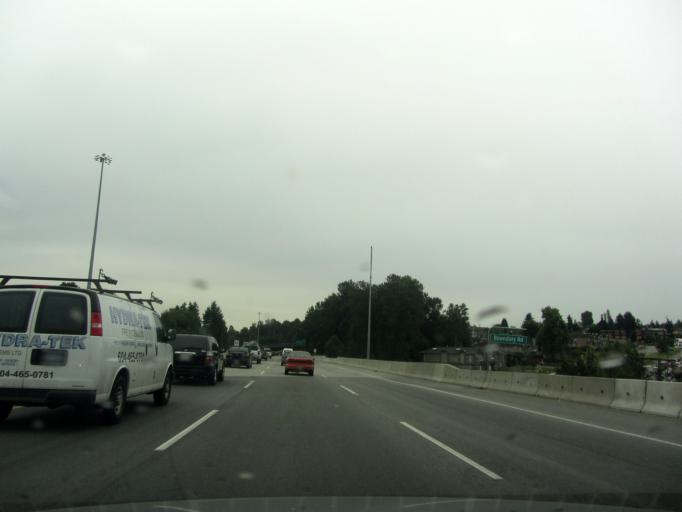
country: CA
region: British Columbia
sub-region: Fraser Valley Regional District
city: North Vancouver
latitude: 49.2693
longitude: -123.0416
